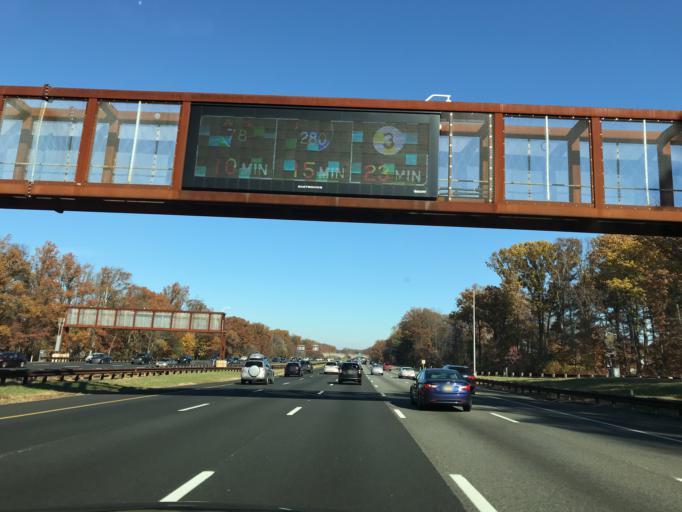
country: US
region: New Jersey
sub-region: Middlesex County
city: Iselin
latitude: 40.5919
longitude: -74.3236
